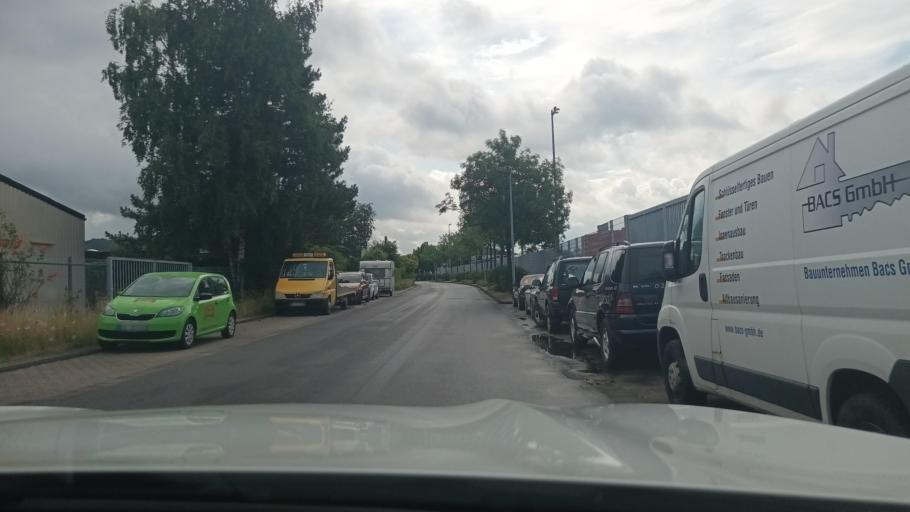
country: DE
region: North Rhine-Westphalia
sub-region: Regierungsbezirk Koln
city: Stossdorf
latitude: 50.7842
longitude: 7.2663
